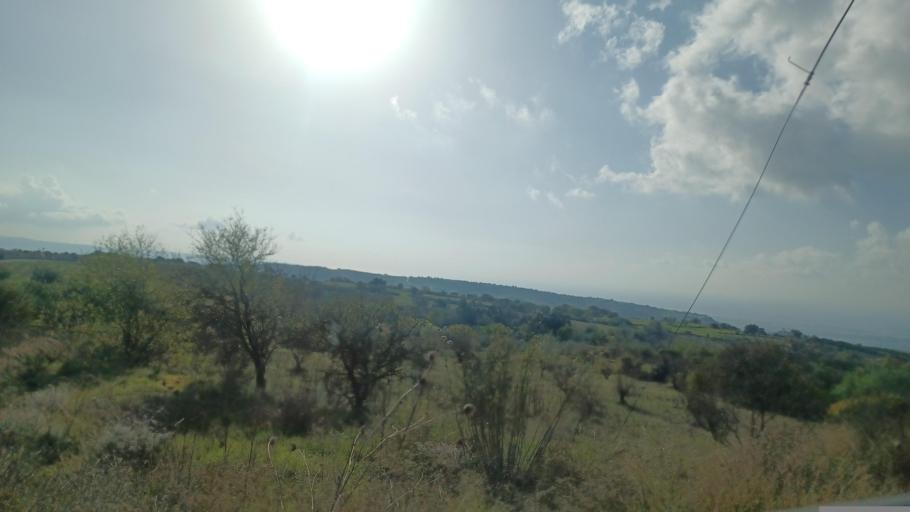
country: CY
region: Pafos
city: Mesogi
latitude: 34.8044
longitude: 32.4904
